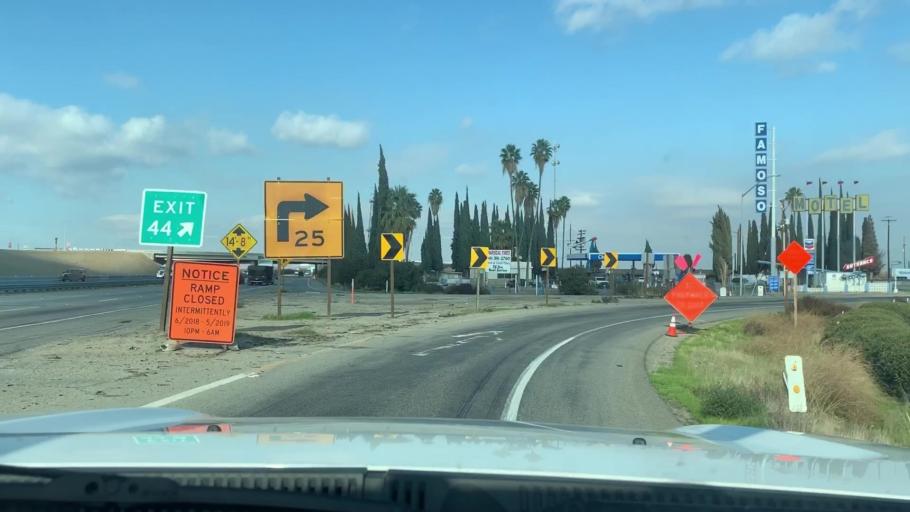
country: US
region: California
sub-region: Kern County
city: McFarland
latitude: 35.5995
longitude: -119.2103
